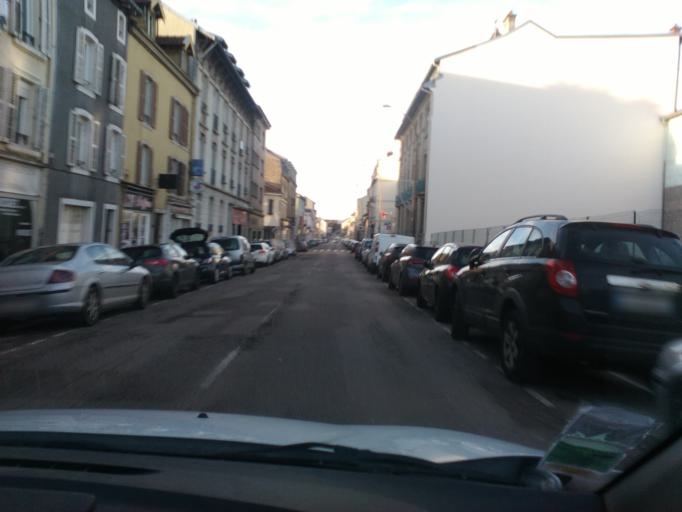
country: FR
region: Lorraine
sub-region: Departement des Vosges
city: Epinal
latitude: 48.1806
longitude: 6.4448
